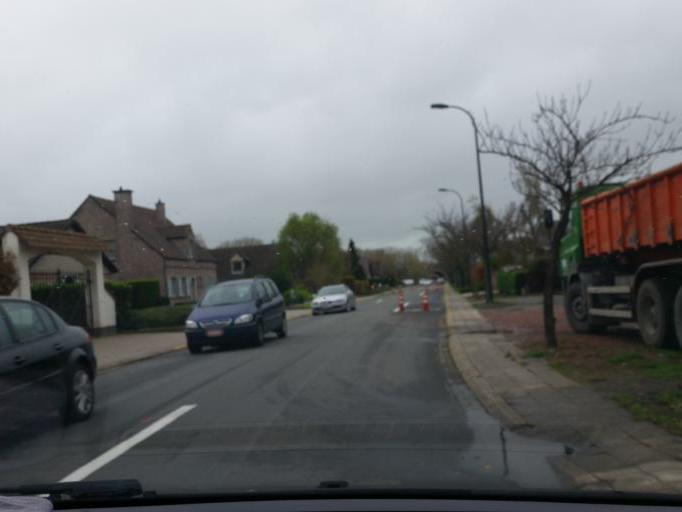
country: BE
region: Flanders
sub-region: Provincie Vlaams-Brabant
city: Vilvoorde
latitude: 50.9479
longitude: 4.4550
